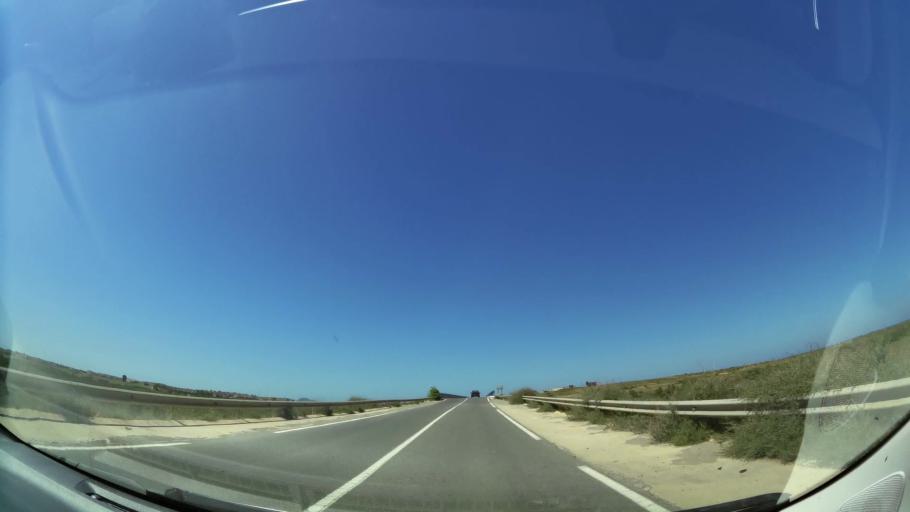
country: MA
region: Oriental
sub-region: Berkane-Taourirt
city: Madagh
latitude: 35.1068
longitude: -2.3612
